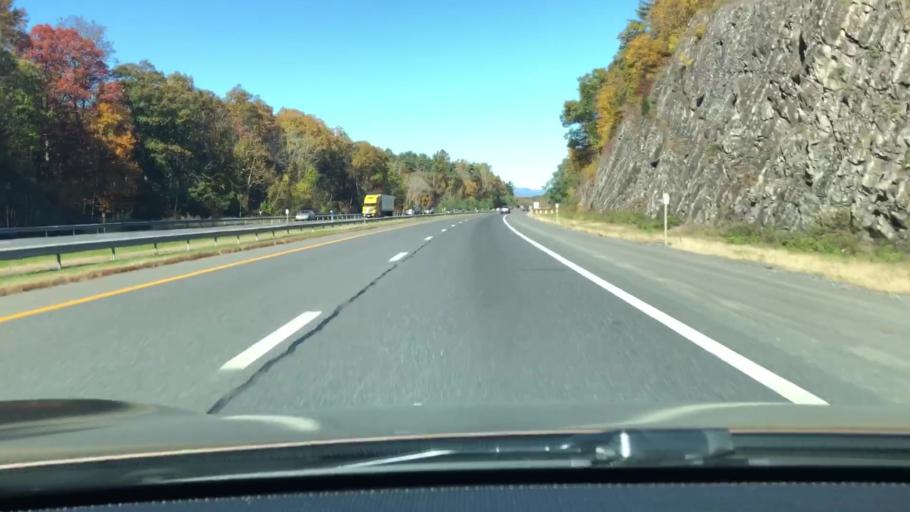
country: US
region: New York
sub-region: Ulster County
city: Rosendale Village
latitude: 41.8707
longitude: -74.0580
